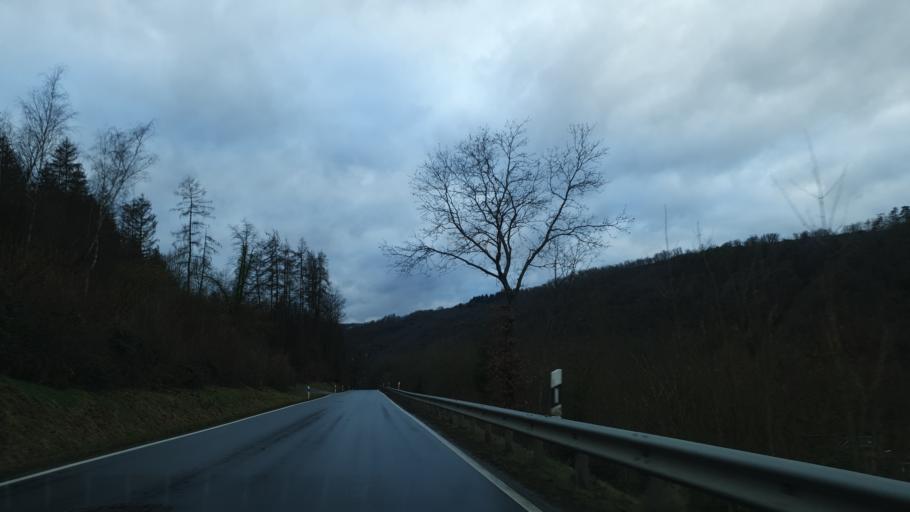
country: DE
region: Rheinland-Pfalz
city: Gutenacker
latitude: 50.3285
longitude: 7.9269
